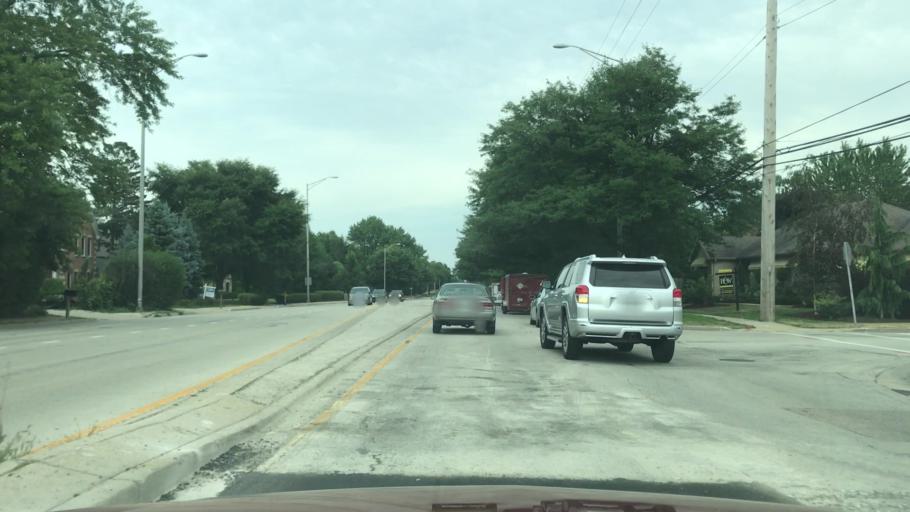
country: US
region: Illinois
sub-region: Cook County
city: Arlington Heights
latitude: 42.0665
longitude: -87.9789
